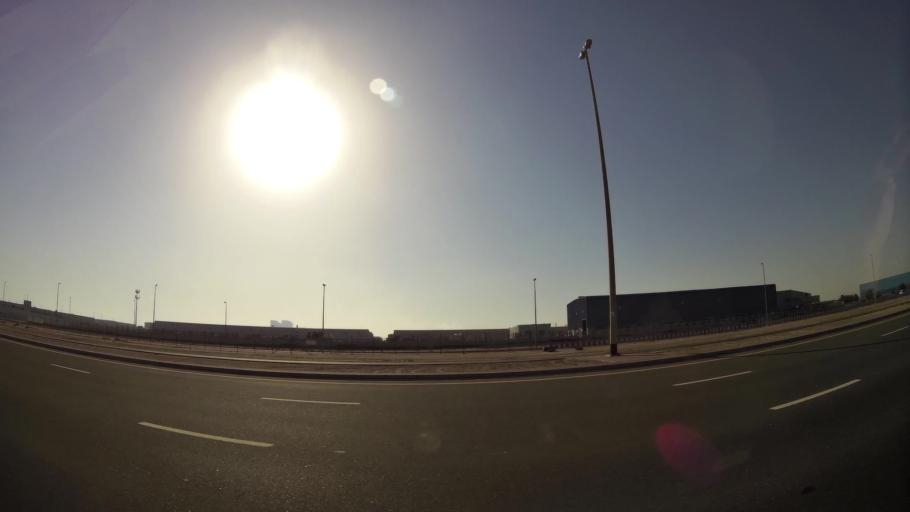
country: AE
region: Dubai
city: Dubai
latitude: 24.9600
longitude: 55.1027
